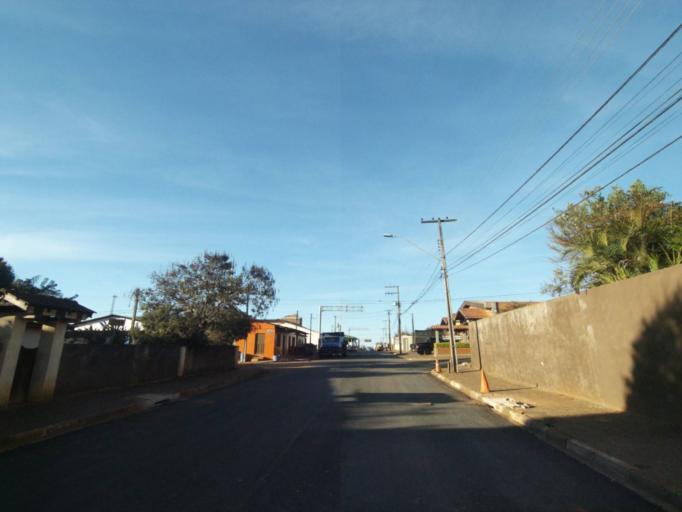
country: BR
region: Parana
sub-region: Tibagi
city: Tibagi
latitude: -24.5200
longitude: -50.4135
